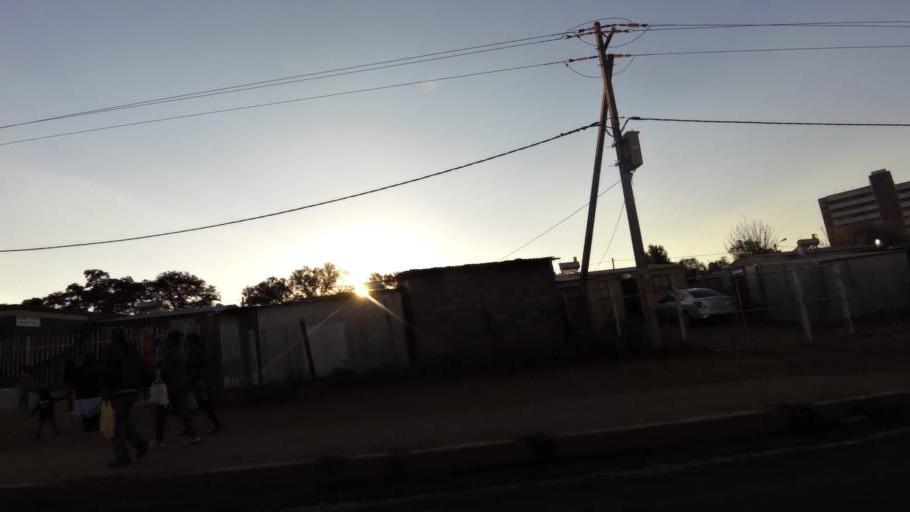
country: ZA
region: Gauteng
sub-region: City of Johannesburg Metropolitan Municipality
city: Johannesburg
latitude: -26.1837
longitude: 27.9615
